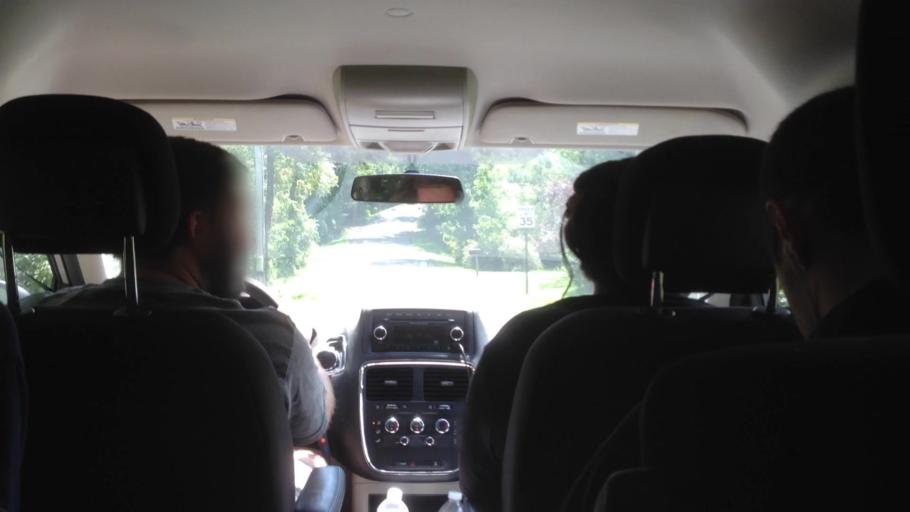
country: US
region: New York
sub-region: Dutchess County
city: Tivoli
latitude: 42.1125
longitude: -73.8928
